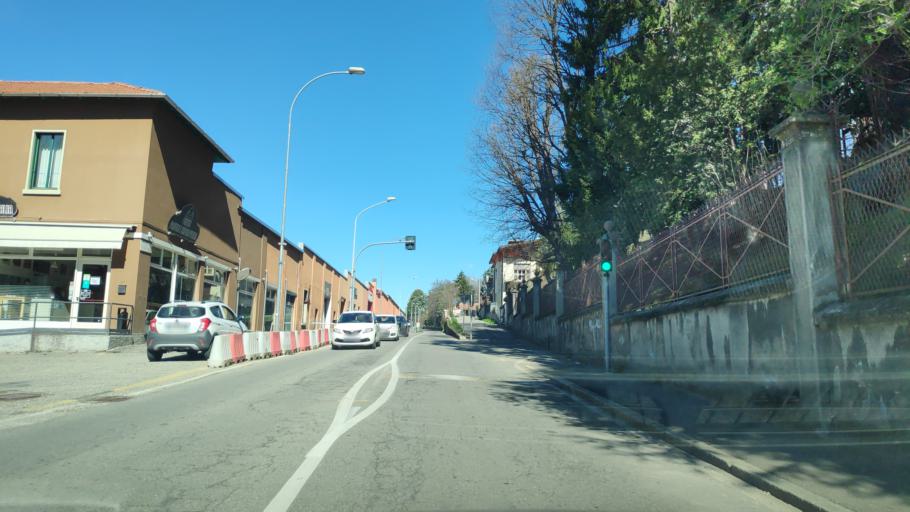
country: IT
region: Lombardy
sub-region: Provincia di Varese
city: Cassano Magnago
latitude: 45.6761
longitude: 8.8223
